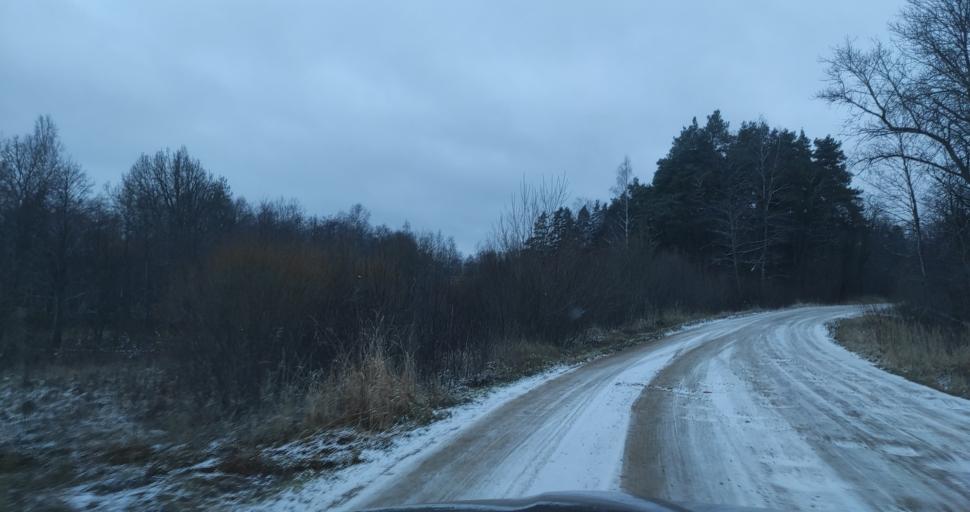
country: LV
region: Kuldigas Rajons
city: Kuldiga
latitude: 56.9810
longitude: 22.0509
